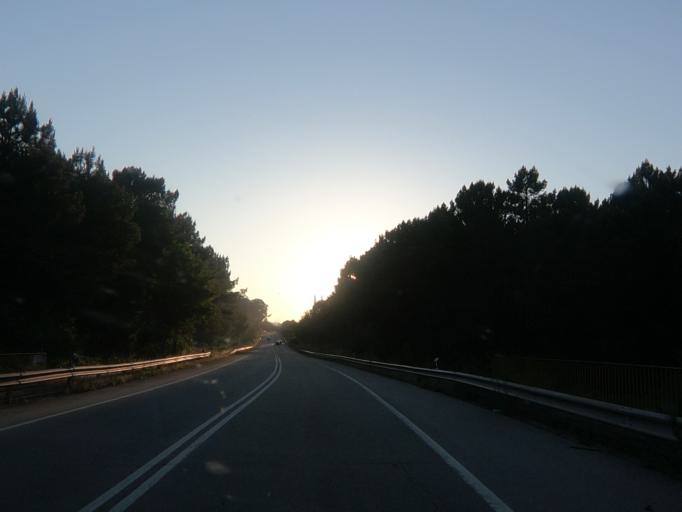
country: PT
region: Viseu
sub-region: Viseu
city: Rio de Loba
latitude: 40.6741
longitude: -7.8628
